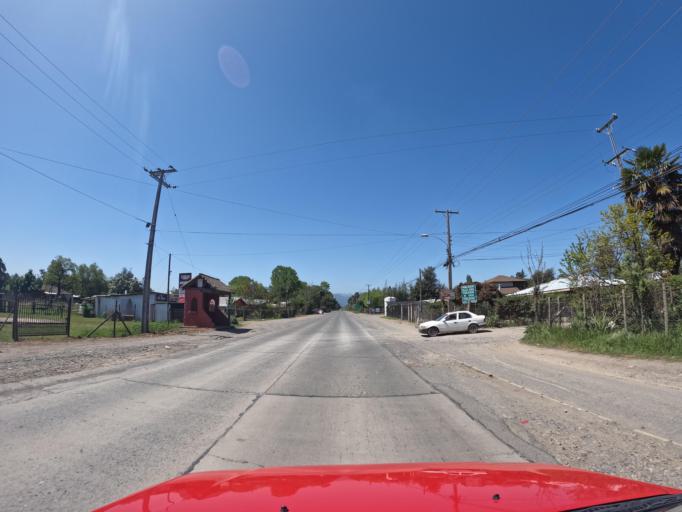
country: CL
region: Maule
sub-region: Provincia de Linares
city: Linares
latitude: -35.8319
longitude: -71.5254
